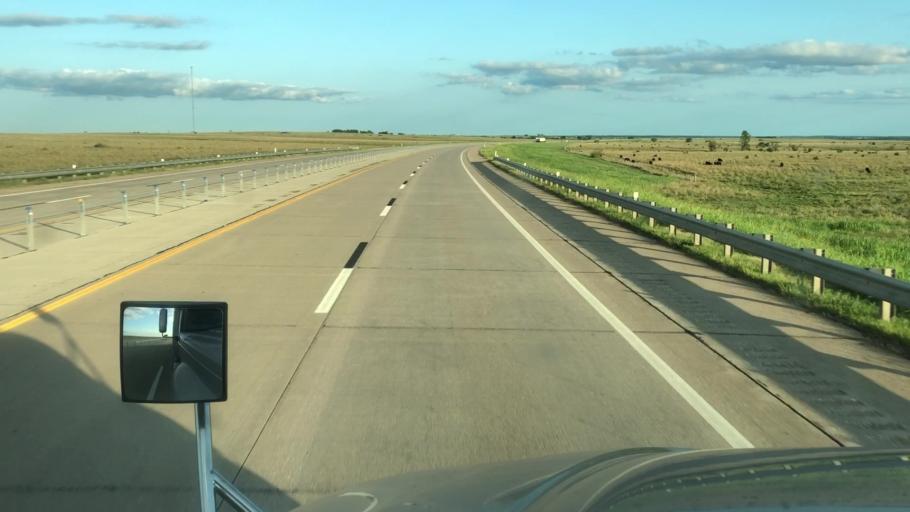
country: US
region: Oklahoma
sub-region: Pawnee County
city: Pawnee
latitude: 36.3735
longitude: -97.0399
